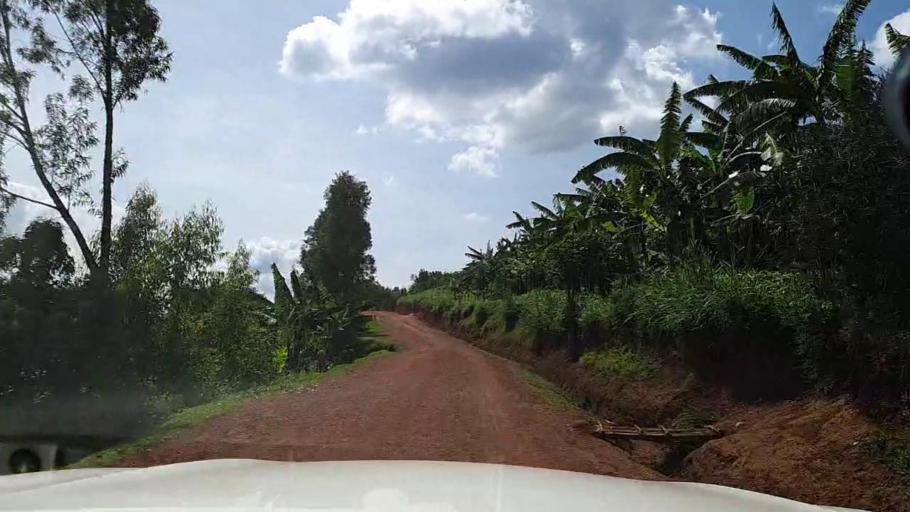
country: RW
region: Southern Province
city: Butare
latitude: -2.7442
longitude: 29.6996
